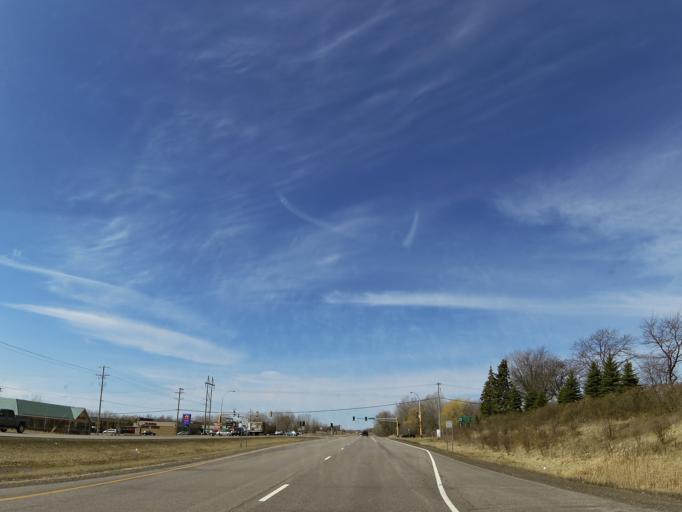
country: US
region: Minnesota
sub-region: Ramsey County
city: North Saint Paul
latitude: 44.9978
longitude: -92.9625
